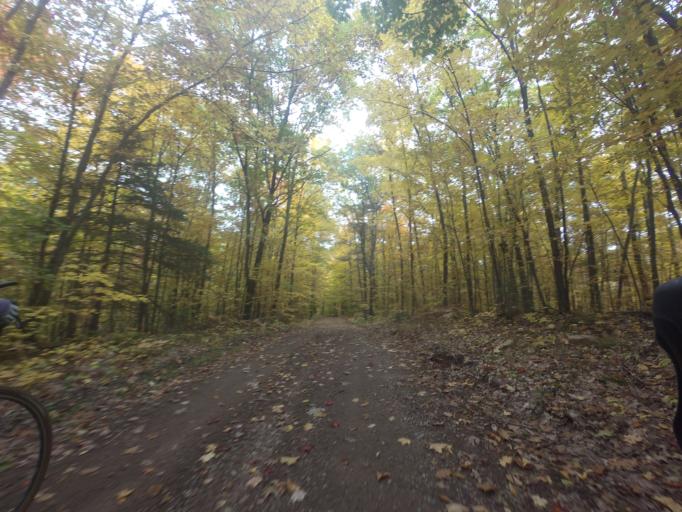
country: CA
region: Ontario
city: Pembroke
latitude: 45.7242
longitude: -77.2259
